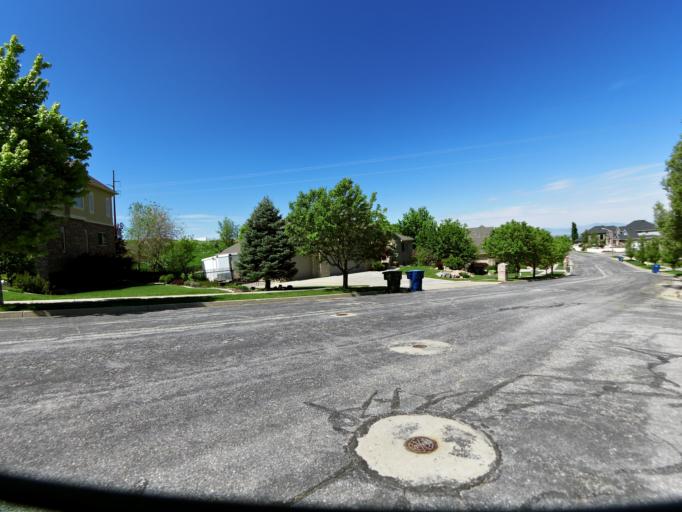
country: US
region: Utah
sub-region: Weber County
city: Uintah
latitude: 41.1744
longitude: -111.9389
